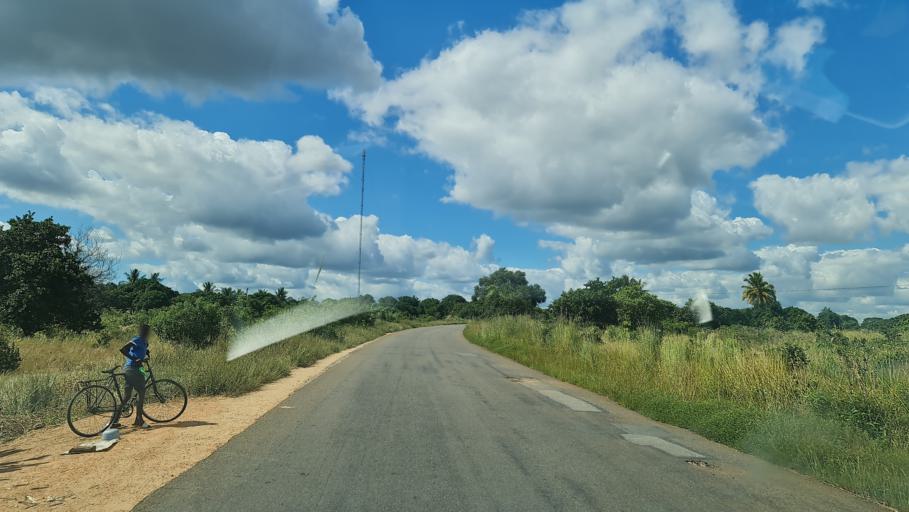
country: MZ
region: Zambezia
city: Quelimane
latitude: -17.5069
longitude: 36.2425
